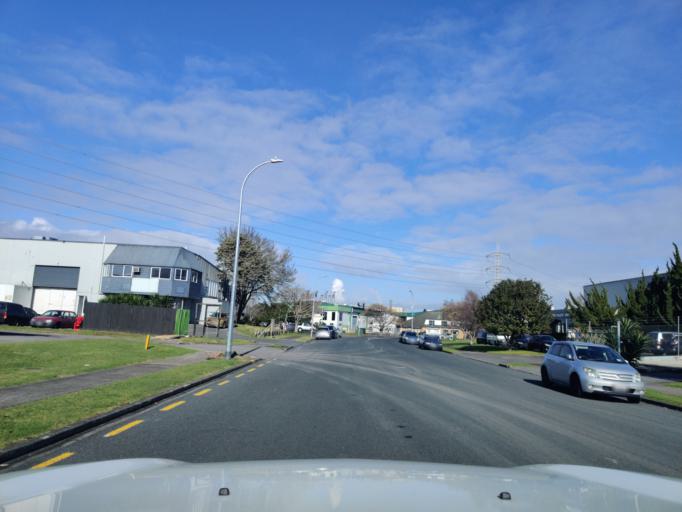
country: NZ
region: Auckland
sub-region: Auckland
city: Manukau City
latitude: -36.9406
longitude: 174.8817
